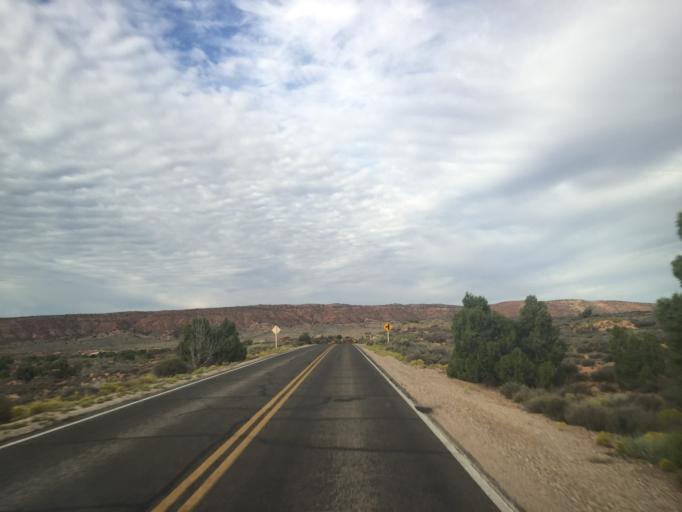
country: US
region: Utah
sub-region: Grand County
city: Moab
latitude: 38.7432
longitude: -109.5711
